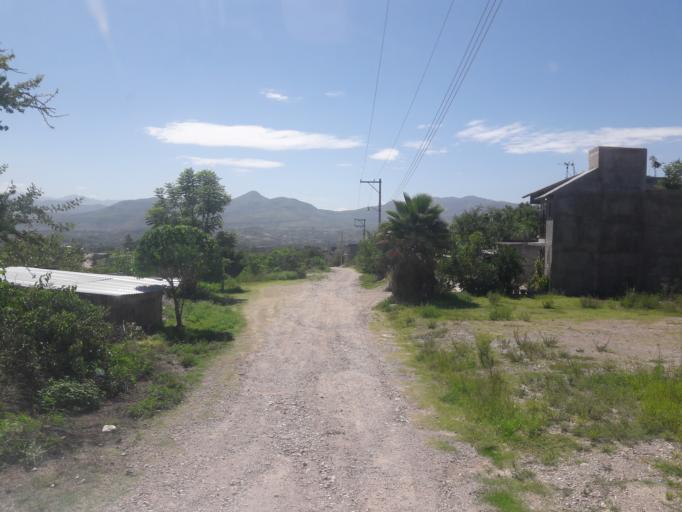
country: MX
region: Oaxaca
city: Ciudad de Huajuapam de Leon
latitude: 17.7955
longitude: -97.7980
